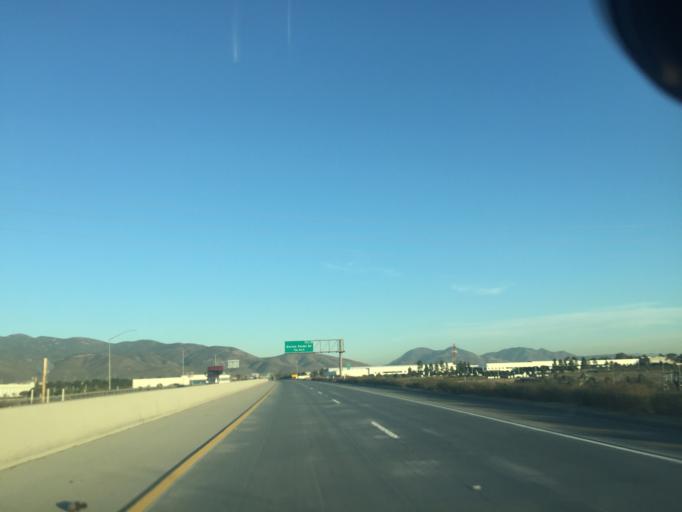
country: MX
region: Baja California
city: Tijuana
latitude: 32.5641
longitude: -116.9467
